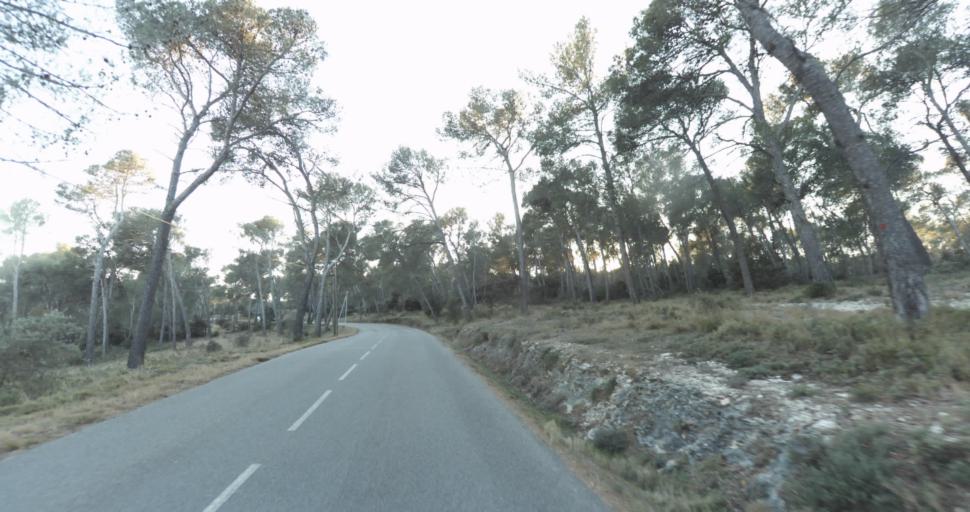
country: FR
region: Provence-Alpes-Cote d'Azur
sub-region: Departement des Bouches-du-Rhone
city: Barbentane
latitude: 43.8820
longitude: 4.7355
